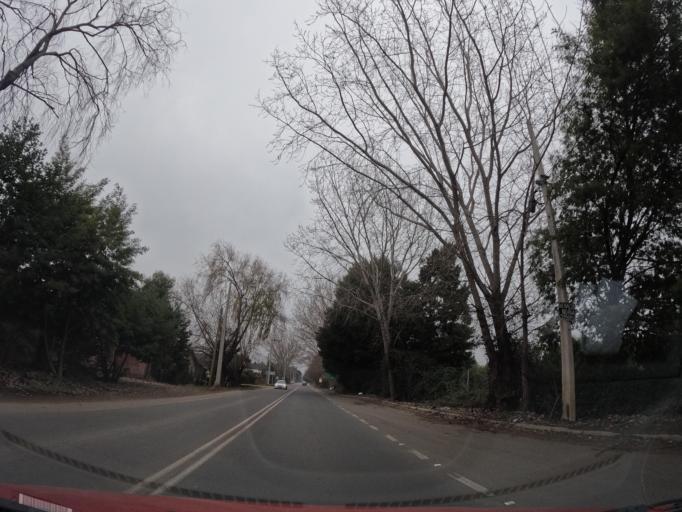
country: CL
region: Maule
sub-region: Provincia de Talca
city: San Clemente
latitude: -35.5595
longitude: -71.4629
